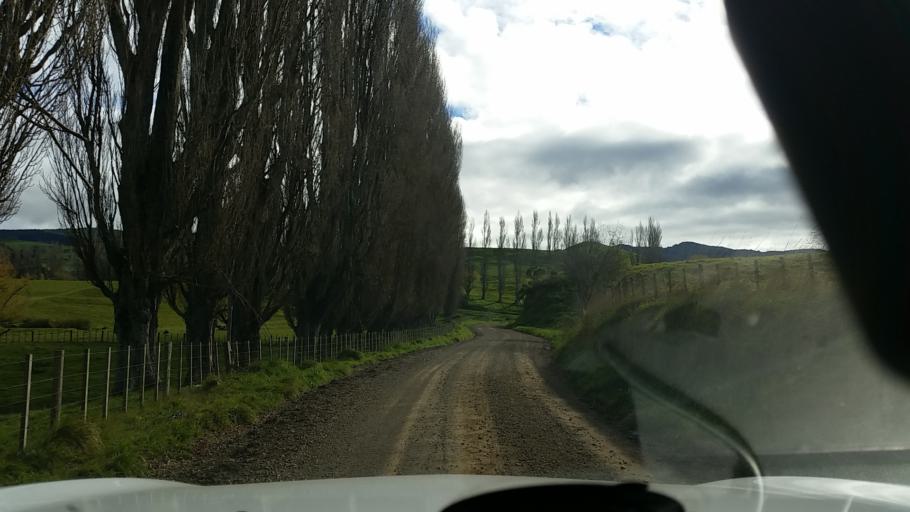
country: NZ
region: Hawke's Bay
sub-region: Napier City
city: Napier
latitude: -39.1037
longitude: 176.8823
